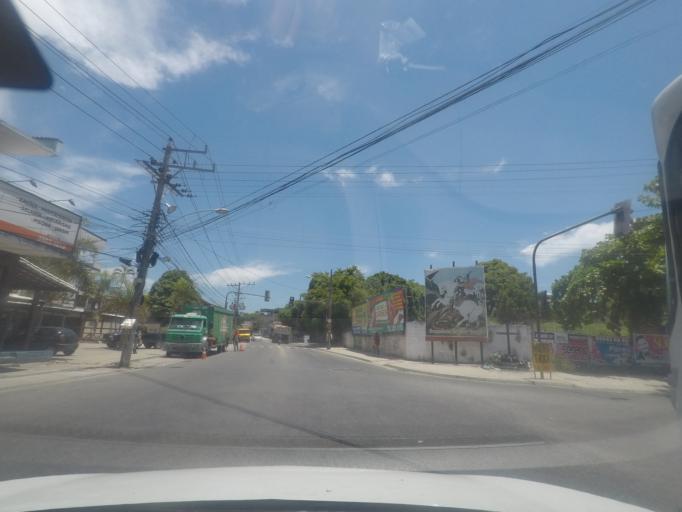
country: BR
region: Rio de Janeiro
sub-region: Itaguai
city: Itaguai
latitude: -22.9272
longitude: -43.6908
